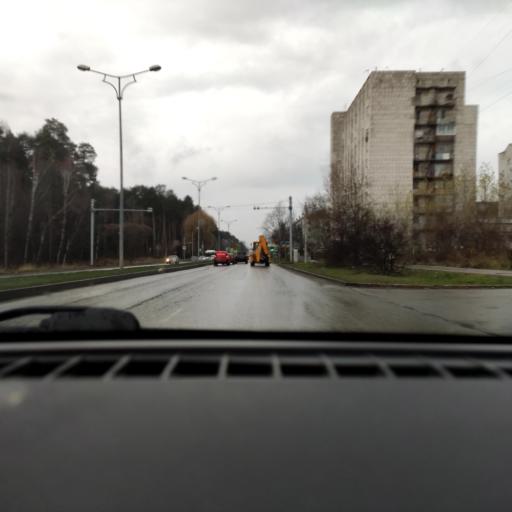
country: RU
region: Perm
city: Kondratovo
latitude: 58.0169
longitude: 55.9827
